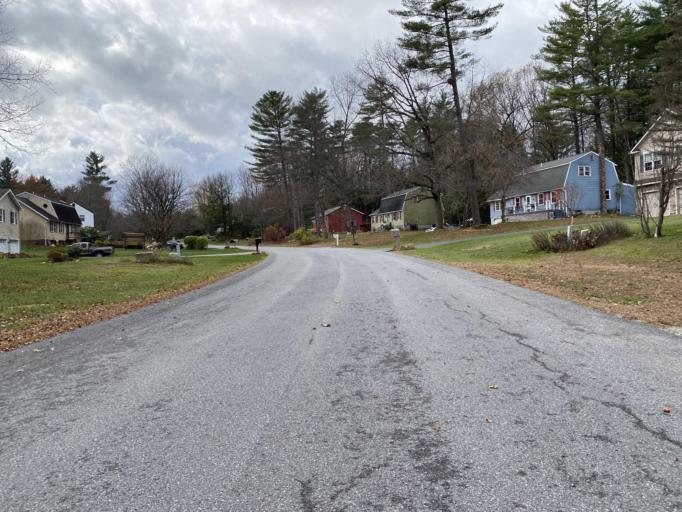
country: US
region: New York
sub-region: Saratoga County
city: Milton
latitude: 43.0985
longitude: -73.9037
